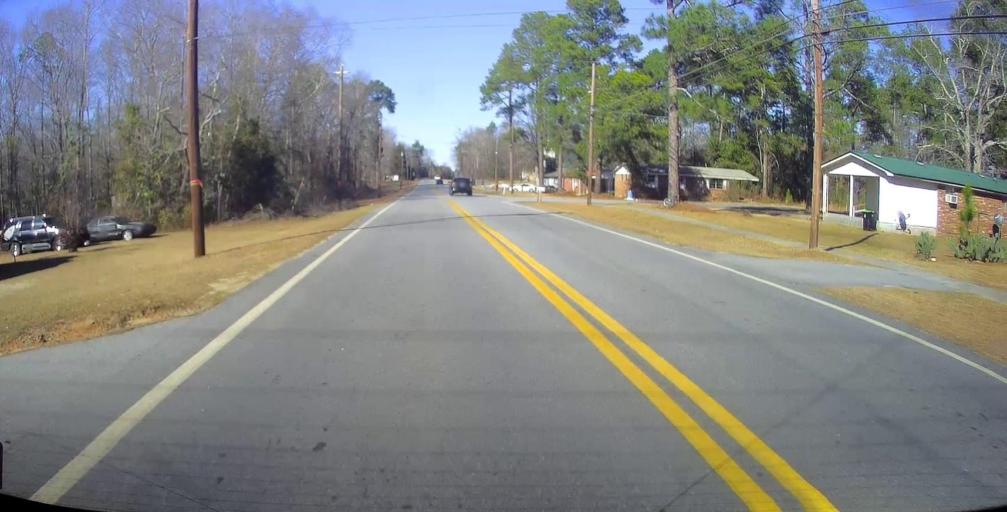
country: US
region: Georgia
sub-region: Taylor County
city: Butler
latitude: 32.5586
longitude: -84.2247
